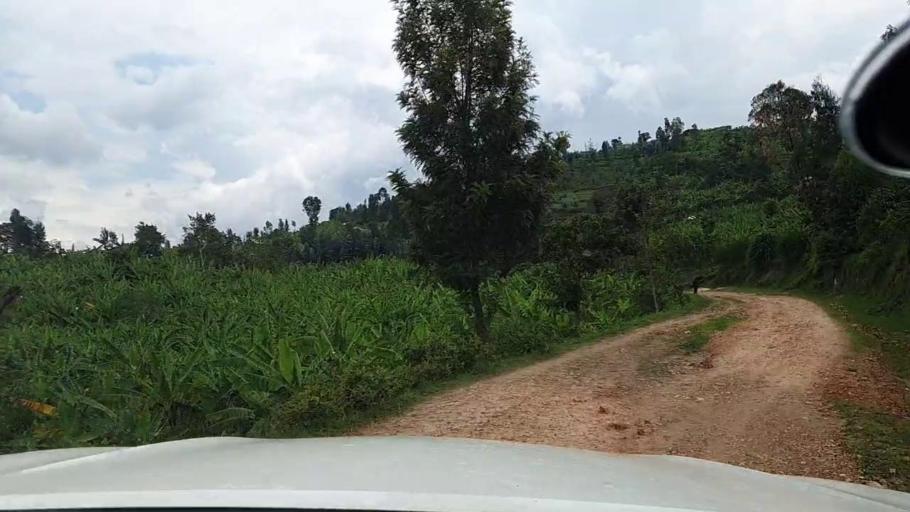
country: RW
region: Western Province
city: Kibuye
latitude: -2.0761
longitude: 29.4225
